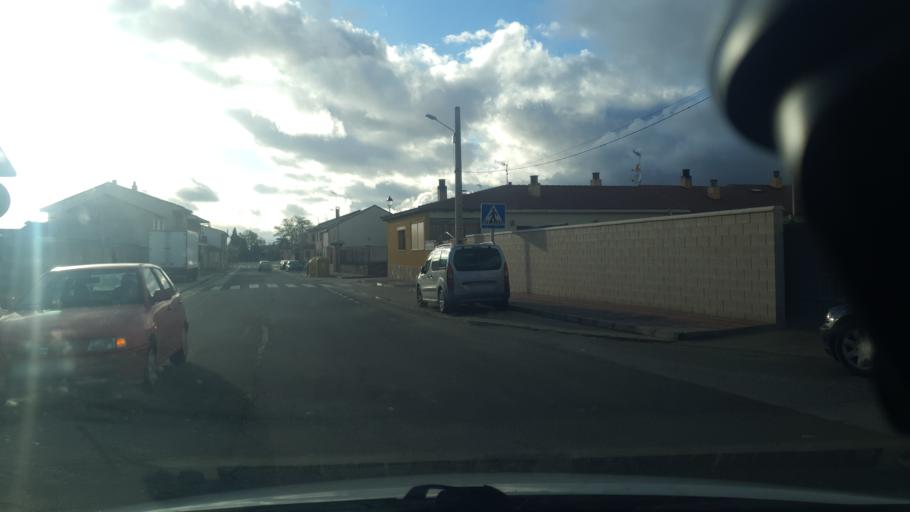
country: ES
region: Castille and Leon
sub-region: Provincia de Segovia
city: Nava de la Asuncion
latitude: 41.1571
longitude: -4.4911
